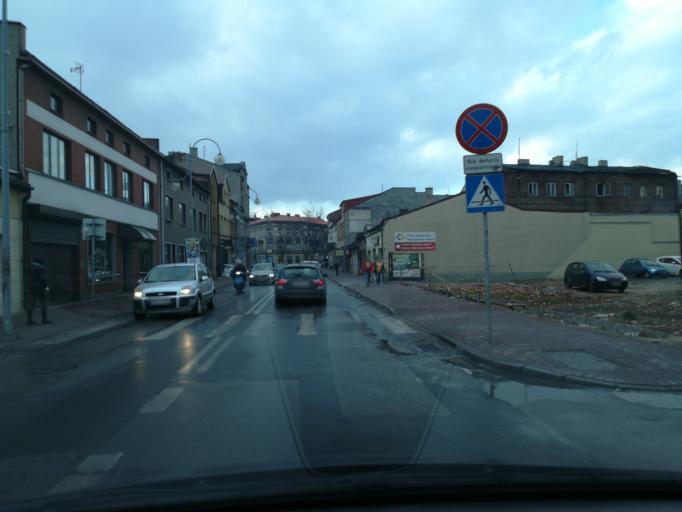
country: PL
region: Lodz Voivodeship
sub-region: Powiat radomszczanski
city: Radomsko
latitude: 51.0683
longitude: 19.4406
